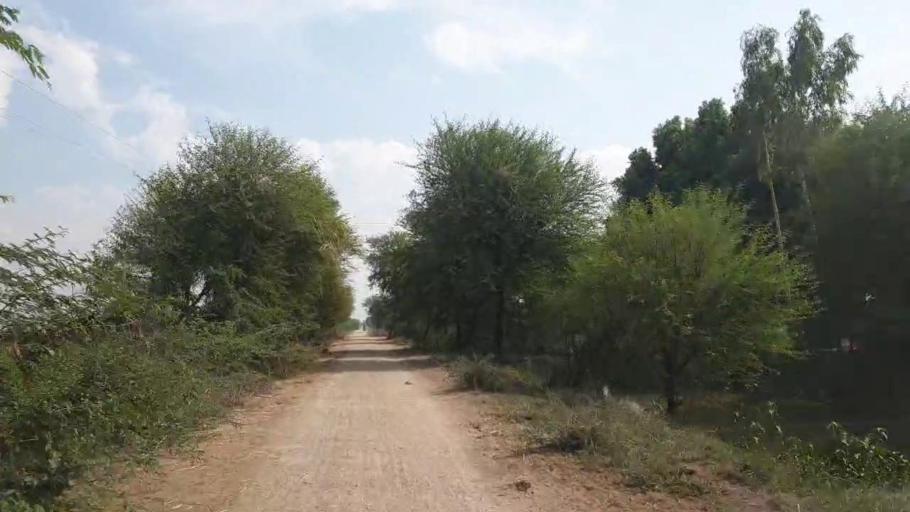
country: PK
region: Sindh
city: Tando Bago
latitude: 24.9290
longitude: 69.0099
